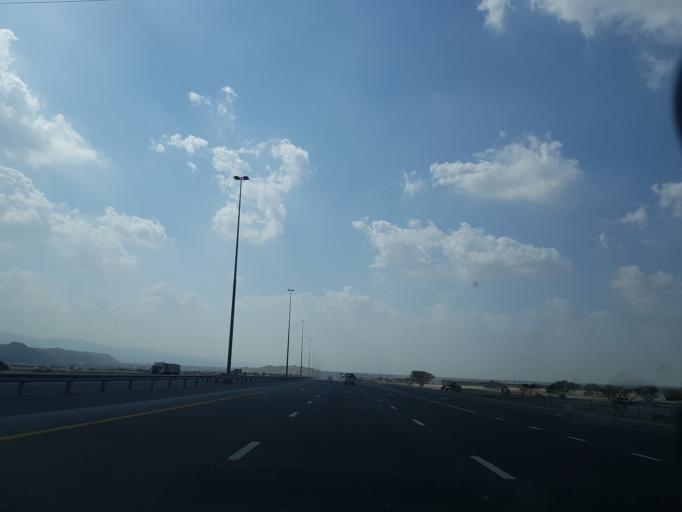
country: AE
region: Ra's al Khaymah
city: Ras al-Khaimah
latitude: 25.7498
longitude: 56.0165
